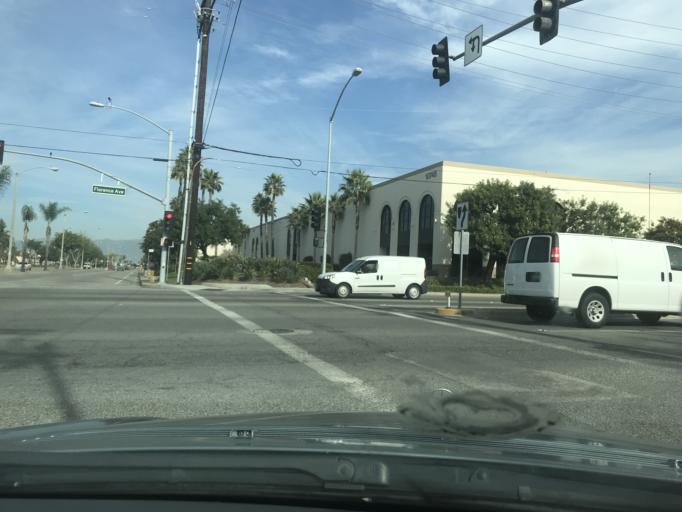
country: US
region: California
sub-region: Los Angeles County
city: Santa Fe Springs
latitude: 33.9353
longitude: -118.0640
